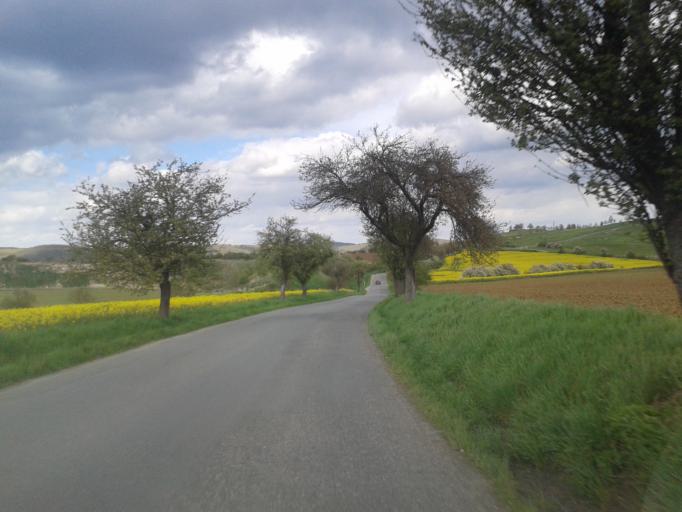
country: CZ
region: Central Bohemia
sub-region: Okres Beroun
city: Lodenice
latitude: 49.9165
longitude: 14.1574
